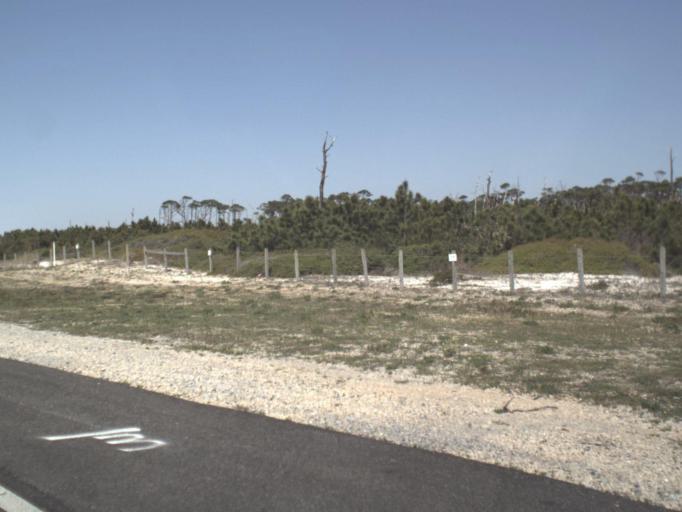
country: US
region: Florida
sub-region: Okaloosa County
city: Destin
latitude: 30.3897
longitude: -86.5278
